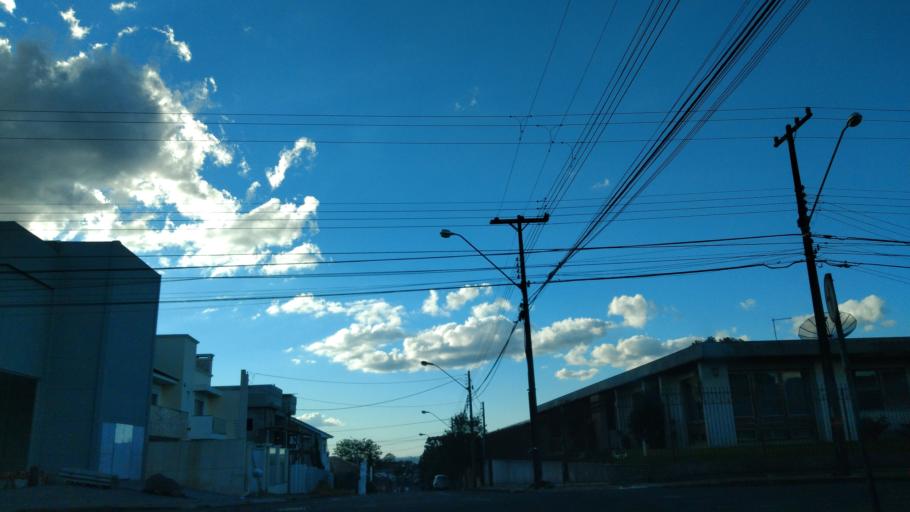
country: BR
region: Parana
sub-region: Guarapuava
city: Guarapuava
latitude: -25.3953
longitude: -51.4740
